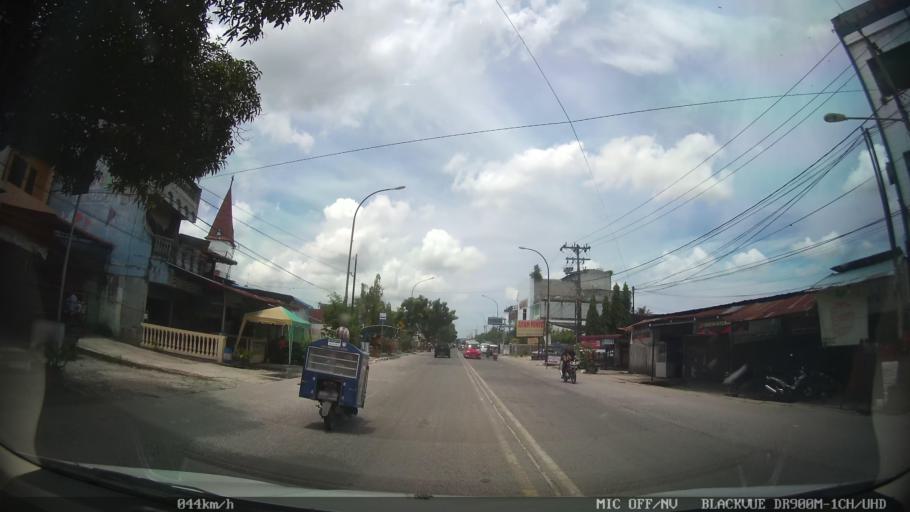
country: ID
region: North Sumatra
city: Percut
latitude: 3.5560
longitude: 98.8797
